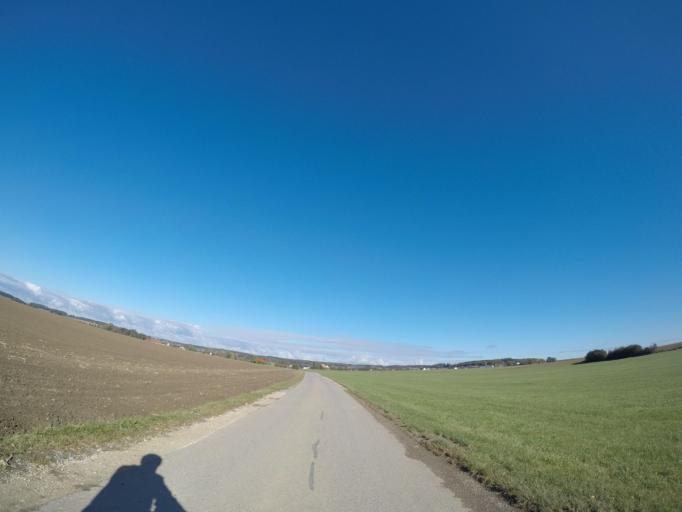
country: DE
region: Baden-Wuerttemberg
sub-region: Tuebingen Region
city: Saulgau
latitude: 48.0389
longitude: 9.5180
